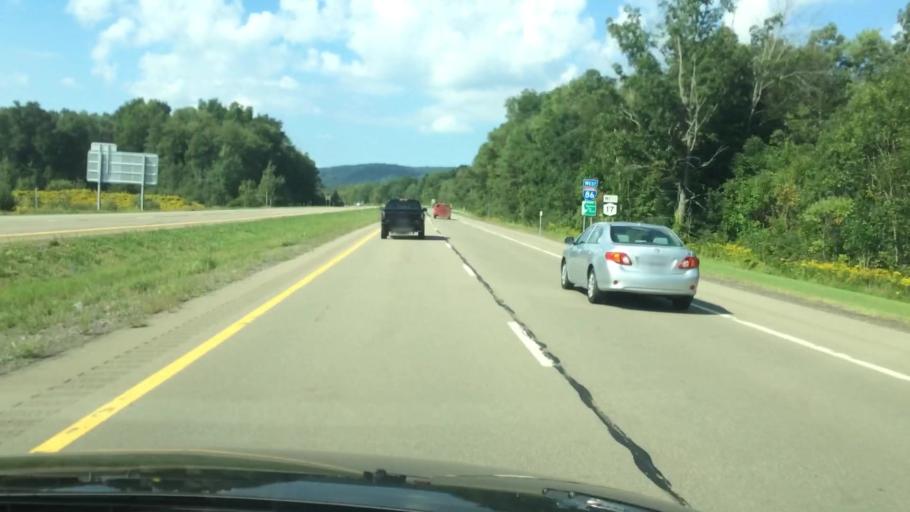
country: US
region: New York
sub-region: Cattaraugus County
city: Salamanca
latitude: 42.1524
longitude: -78.7576
